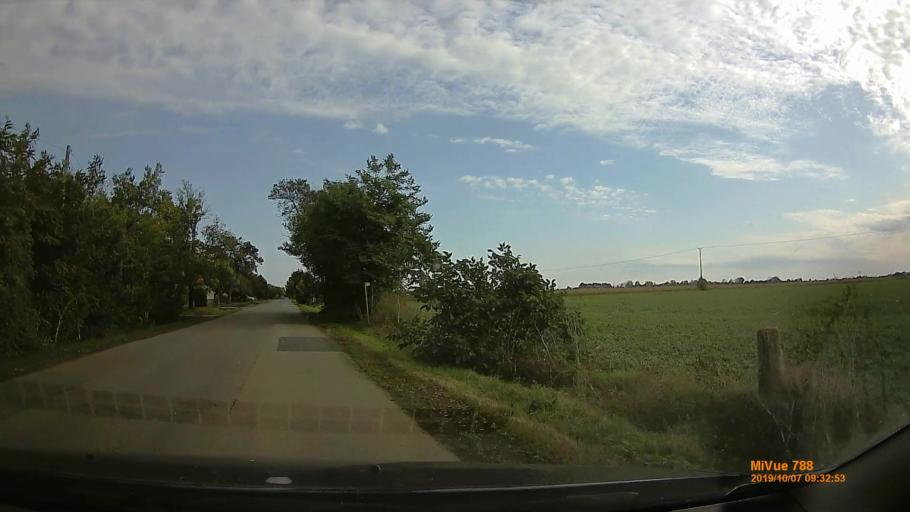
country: HU
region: Bekes
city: Szarvas
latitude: 46.8170
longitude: 20.6535
